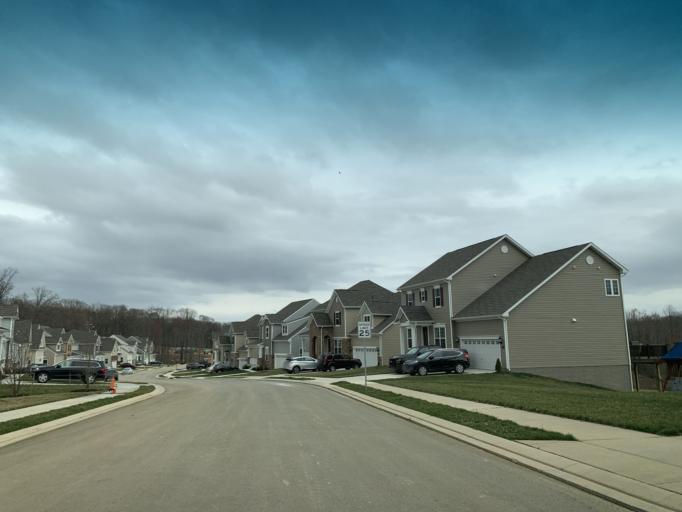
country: US
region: Maryland
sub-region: Harford County
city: Perryman
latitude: 39.5003
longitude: -76.2065
